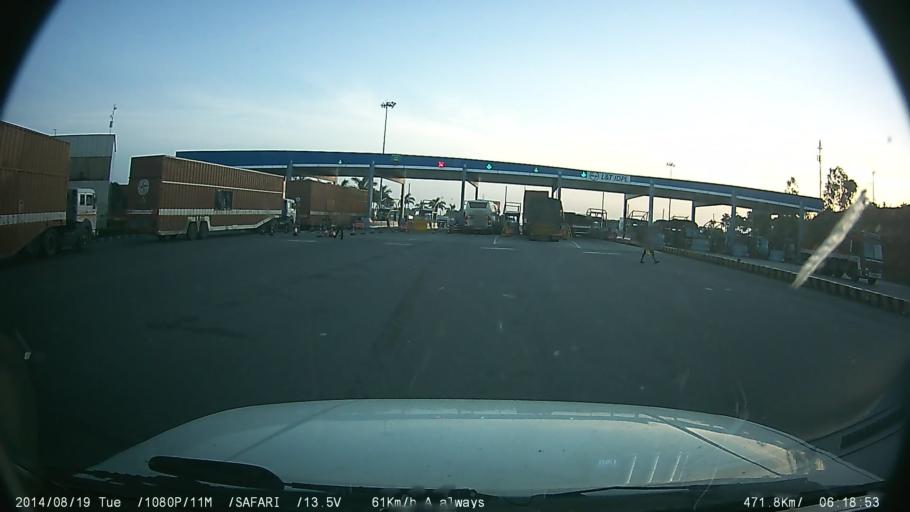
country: IN
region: Tamil Nadu
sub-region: Dharmapuri
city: Dharmapuri
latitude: 12.0056
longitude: 78.0801
